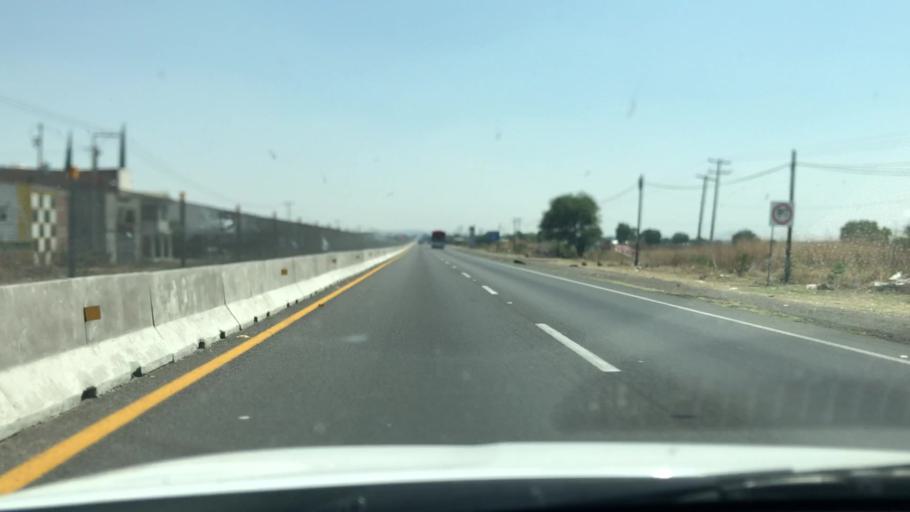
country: MX
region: Guanajuato
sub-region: Abasolo
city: San Bernardo Pena Blanca
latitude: 20.4712
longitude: -101.5037
